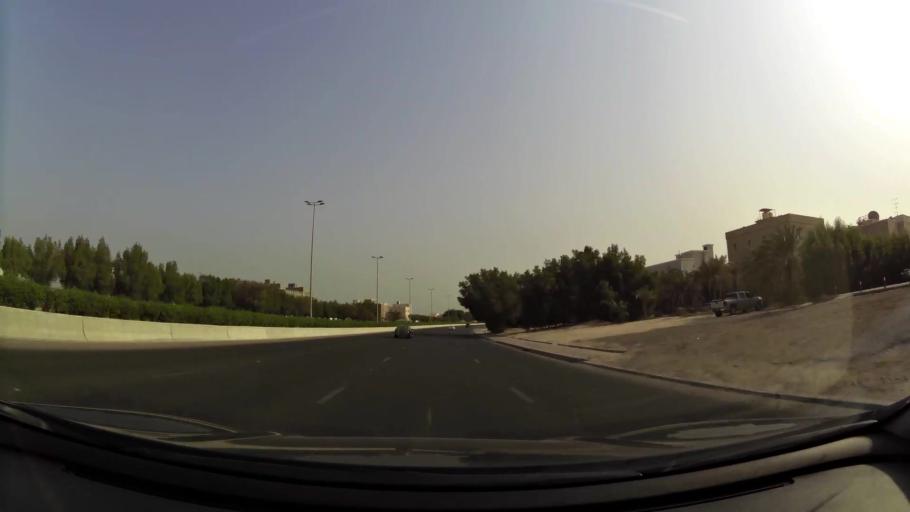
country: KW
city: Al Funaytis
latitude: 29.2223
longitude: 48.0858
